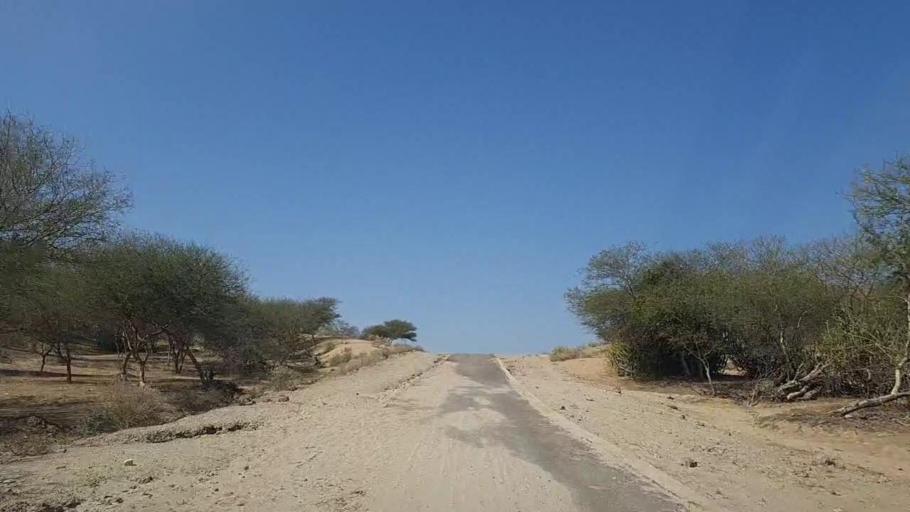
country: PK
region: Sindh
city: Mithi
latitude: 24.7567
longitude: 69.7786
